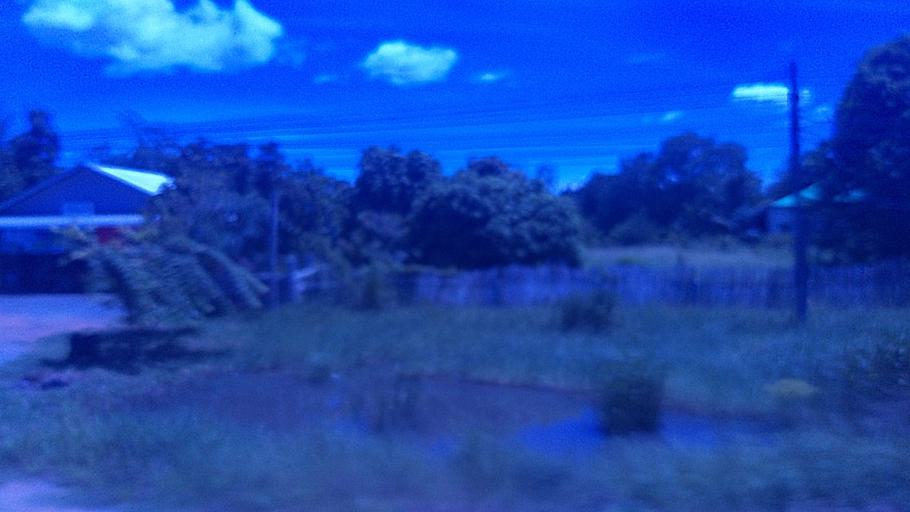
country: TH
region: Chaiyaphum
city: Phu Khiao
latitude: 16.3191
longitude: 102.1980
